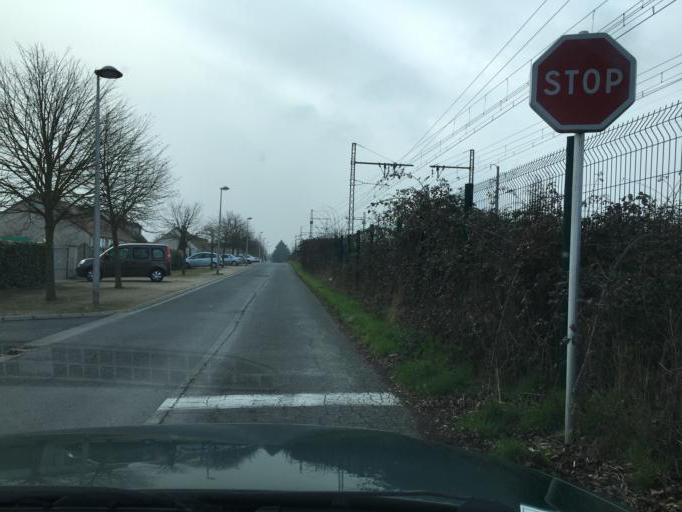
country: FR
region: Centre
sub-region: Departement du Loiret
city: Beaugency
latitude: 47.7853
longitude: 1.6346
